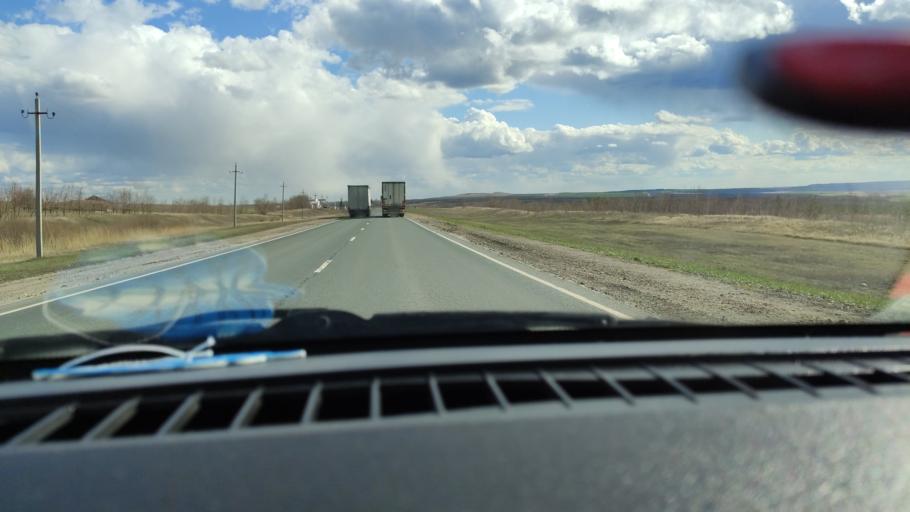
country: RU
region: Saratov
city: Alekseyevka
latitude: 52.2941
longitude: 47.9289
